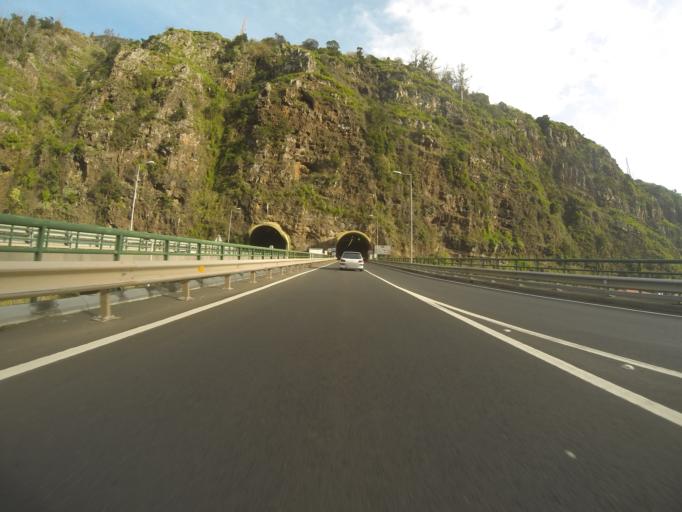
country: PT
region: Madeira
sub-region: Ribeira Brava
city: Campanario
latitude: 32.6826
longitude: -17.0514
